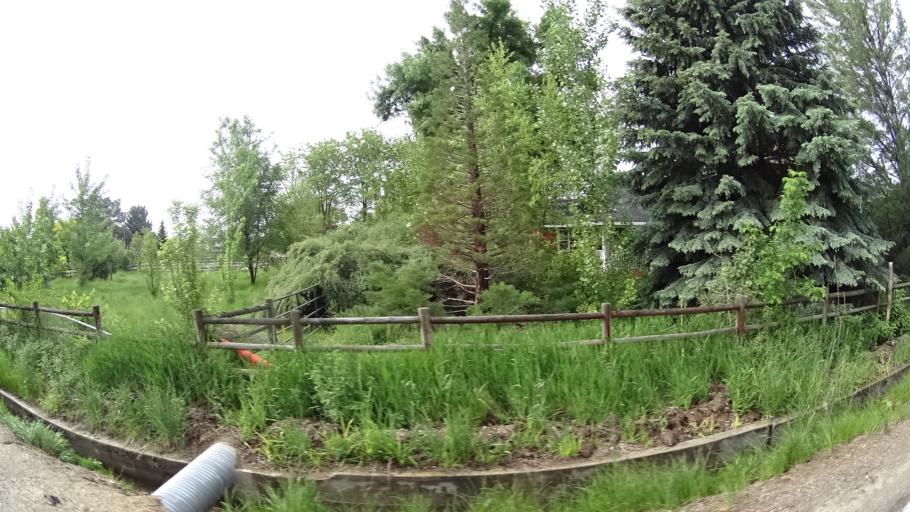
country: US
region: Idaho
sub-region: Ada County
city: Eagle
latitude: 43.7209
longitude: -116.3943
